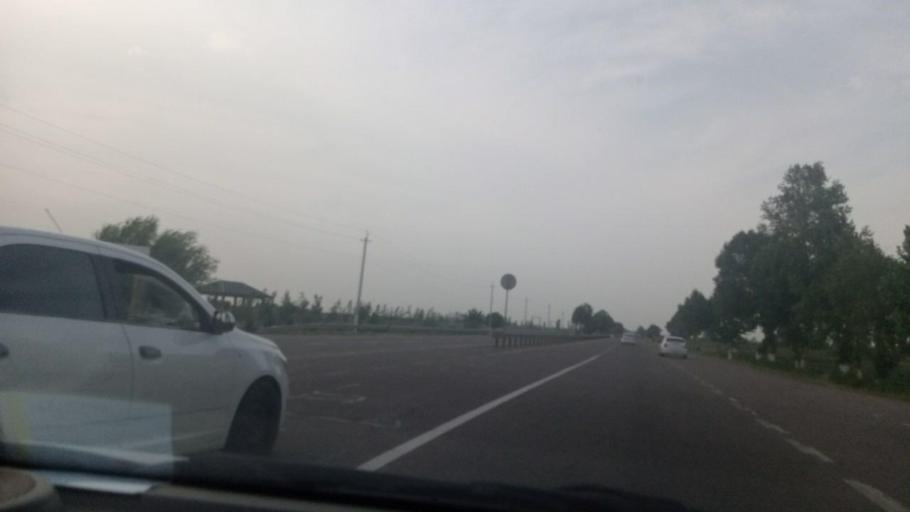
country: UZ
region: Toshkent Shahri
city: Bektemir
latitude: 41.1580
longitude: 69.4225
